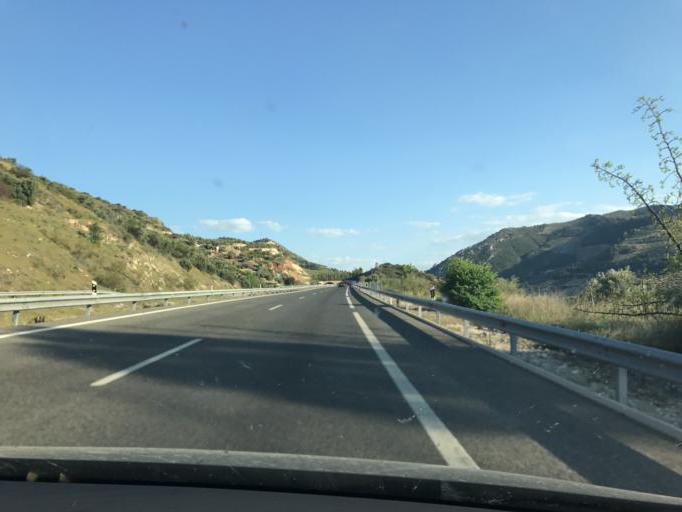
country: ES
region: Andalusia
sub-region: Provincia de Jaen
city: Pegalajar
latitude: 37.7083
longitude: -3.6390
